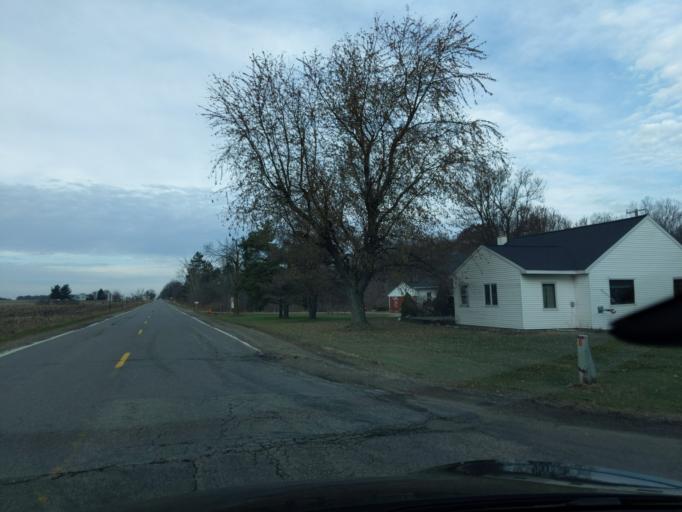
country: US
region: Michigan
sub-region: Ingham County
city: Williamston
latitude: 42.6439
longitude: -84.3638
